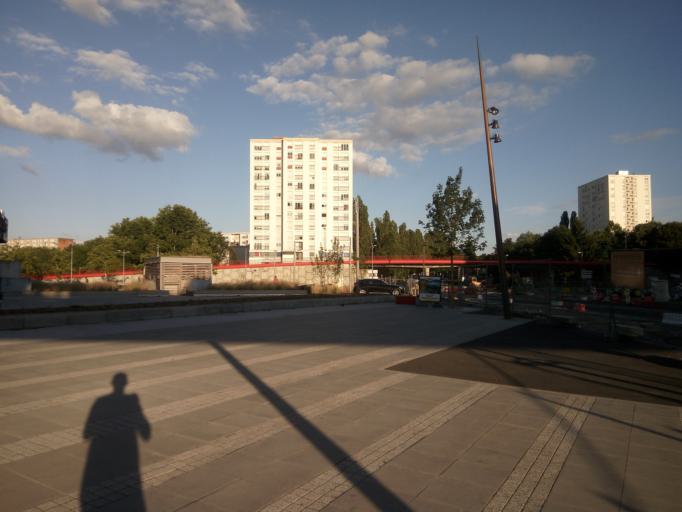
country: FR
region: Lorraine
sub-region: Departement de Meurthe-et-Moselle
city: Vandoeuvre-les-Nancy
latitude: 48.6617
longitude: 6.1747
